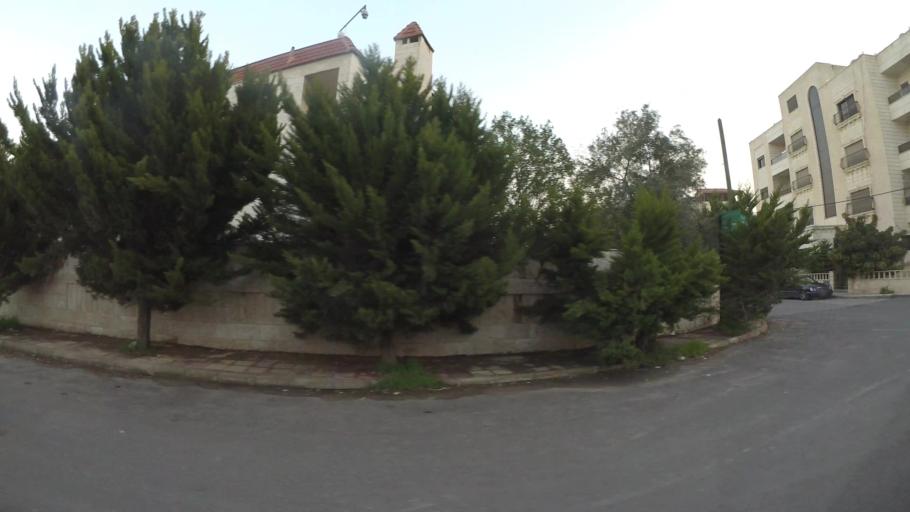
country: JO
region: Amman
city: Amman
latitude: 31.9919
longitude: 35.9607
